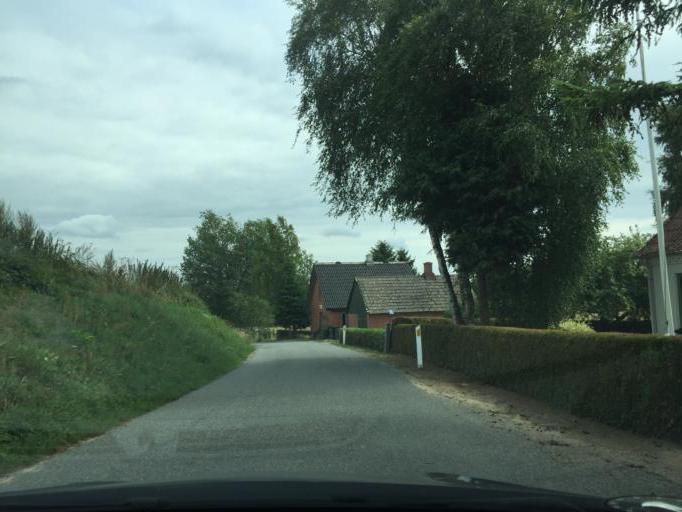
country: DK
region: South Denmark
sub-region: Assens Kommune
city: Vissenbjerg
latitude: 55.3512
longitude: 10.1226
